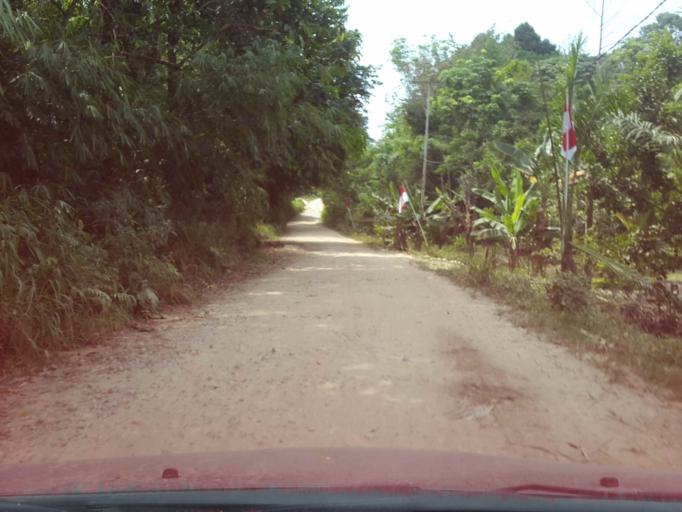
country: MY
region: Sarawak
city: Simanggang
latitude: 0.8398
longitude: 111.7488
